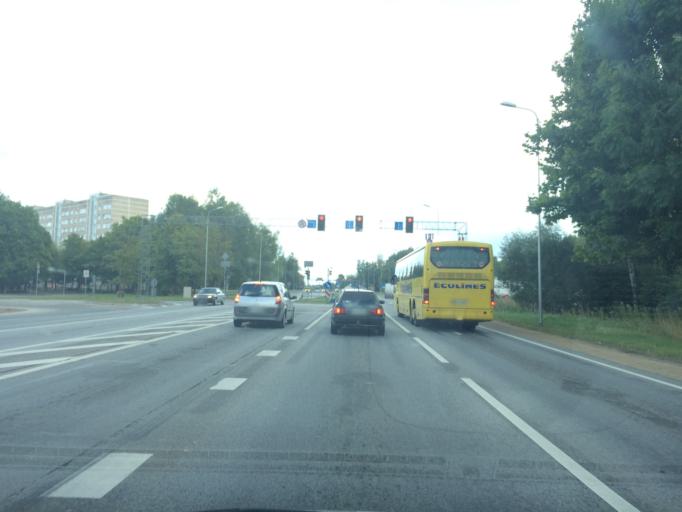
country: LV
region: Salaspils
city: Salaspils
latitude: 56.8529
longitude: 24.3307
